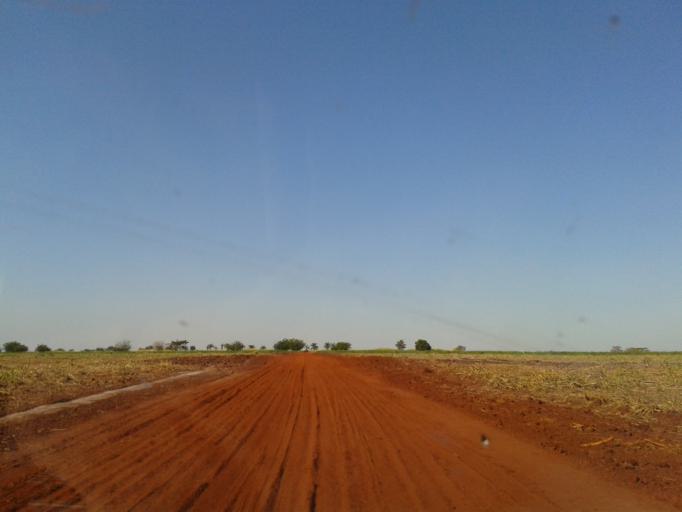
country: BR
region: Minas Gerais
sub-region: Santa Vitoria
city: Santa Vitoria
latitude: -18.7349
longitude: -50.2613
